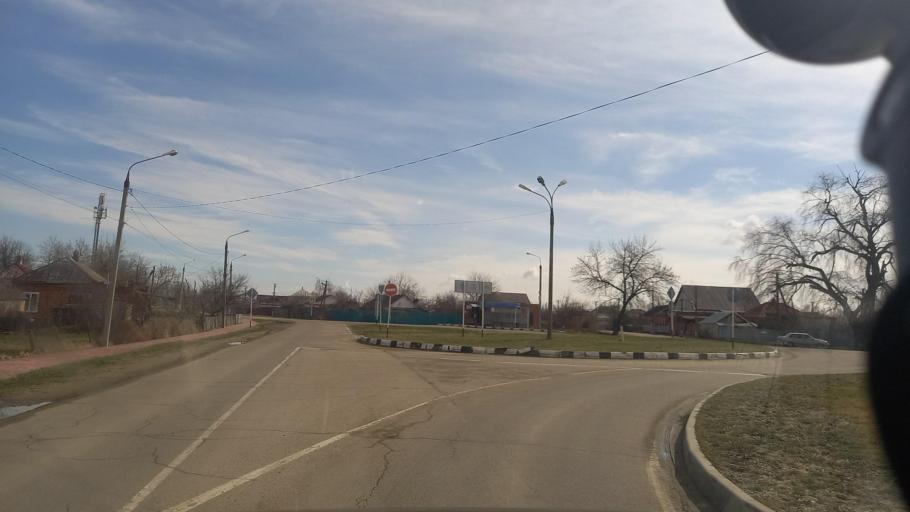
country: RU
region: Adygeya
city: Takhtamukay
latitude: 44.9192
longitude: 39.0041
